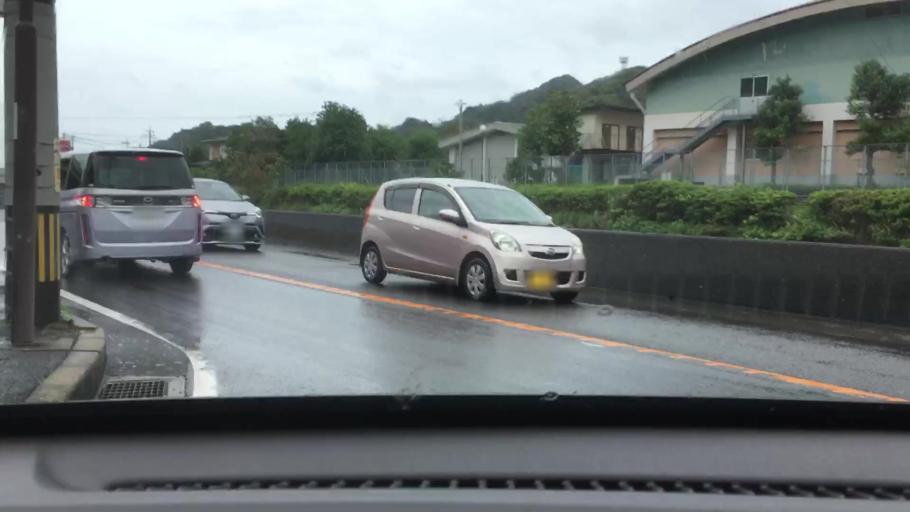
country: JP
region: Nagasaki
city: Togitsu
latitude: 32.8586
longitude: 129.7853
